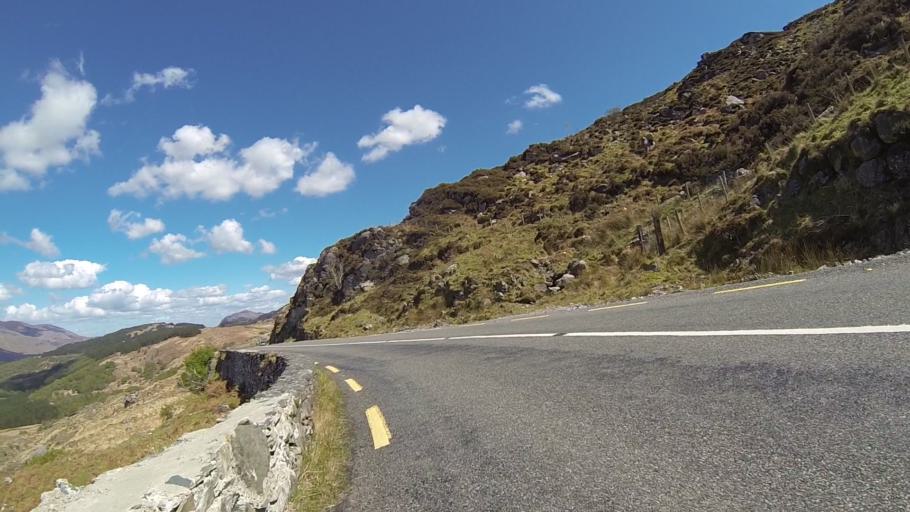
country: IE
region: Munster
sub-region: Ciarrai
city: Kenmare
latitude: 51.9450
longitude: -9.6429
